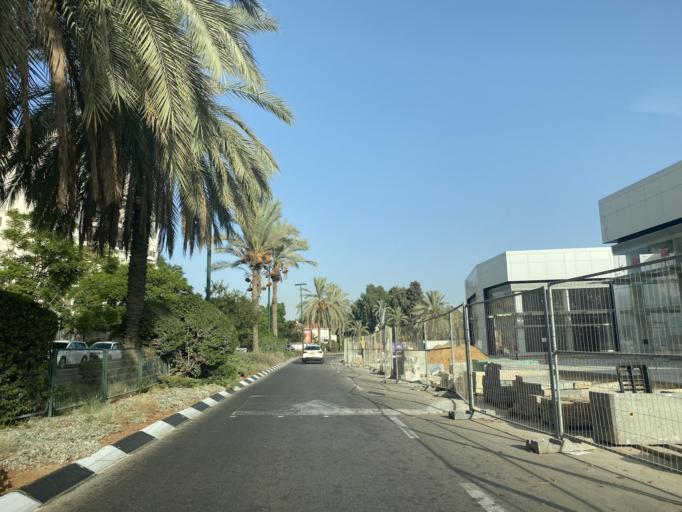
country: IL
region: Central District
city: Kfar Saba
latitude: 32.1634
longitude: 34.9089
